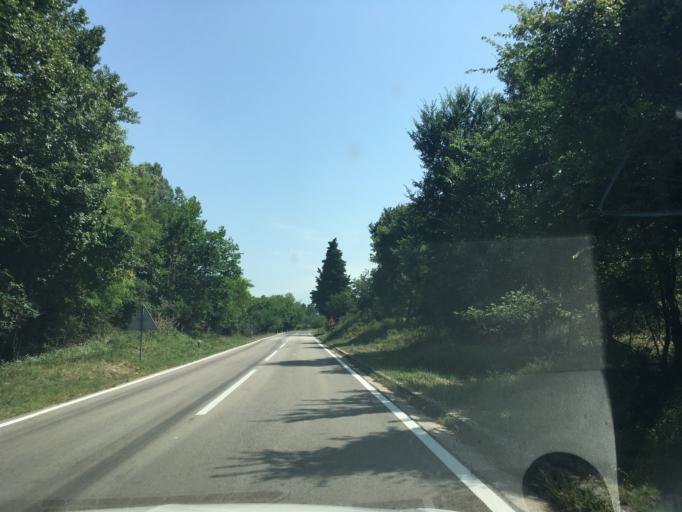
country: HR
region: Sibensko-Kniniska
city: Zaton
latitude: 43.9278
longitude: 15.8124
